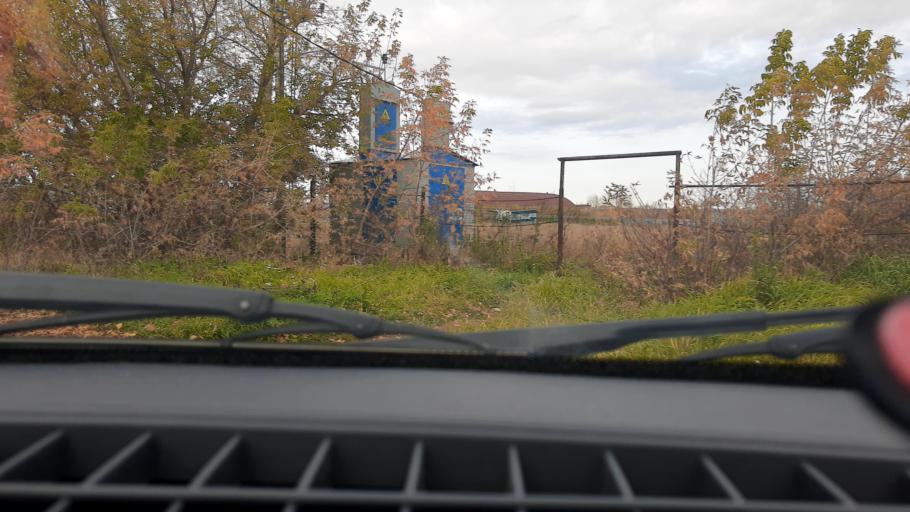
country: RU
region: Bashkortostan
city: Mikhaylovka
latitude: 54.7967
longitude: 55.9426
